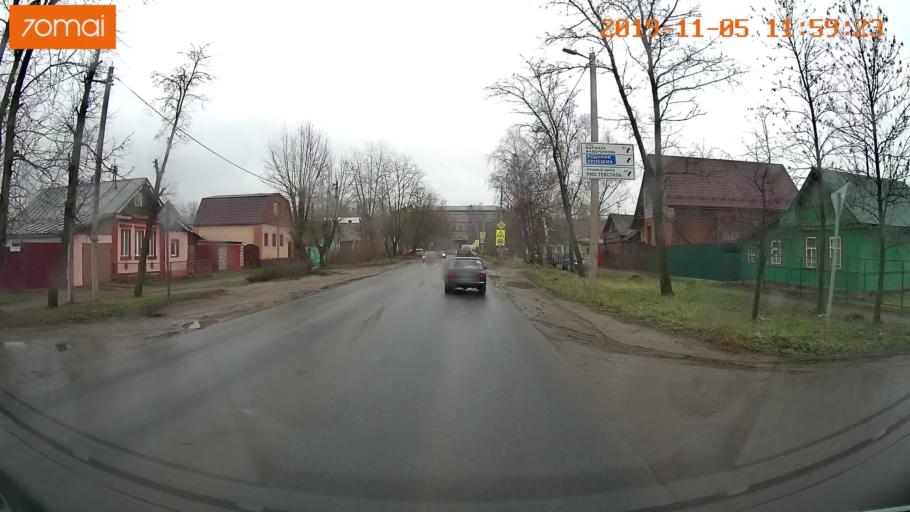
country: RU
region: Ivanovo
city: Kokhma
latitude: 56.9784
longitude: 41.0477
